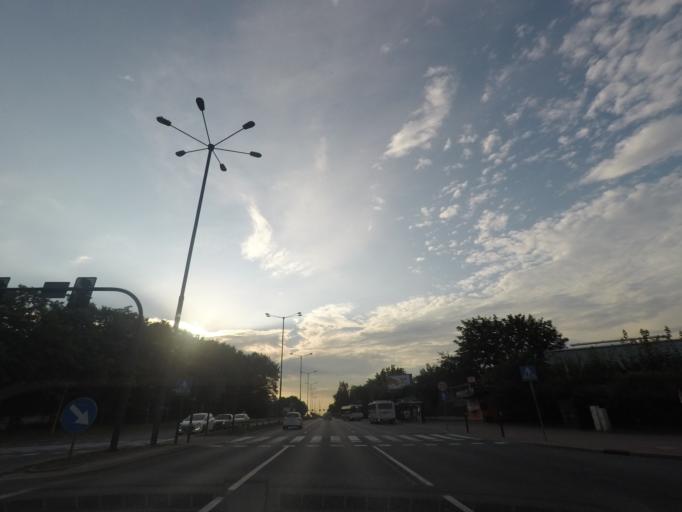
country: PL
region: Lesser Poland Voivodeship
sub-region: Powiat wielicki
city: Czarnochowice
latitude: 50.0103
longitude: 20.0086
